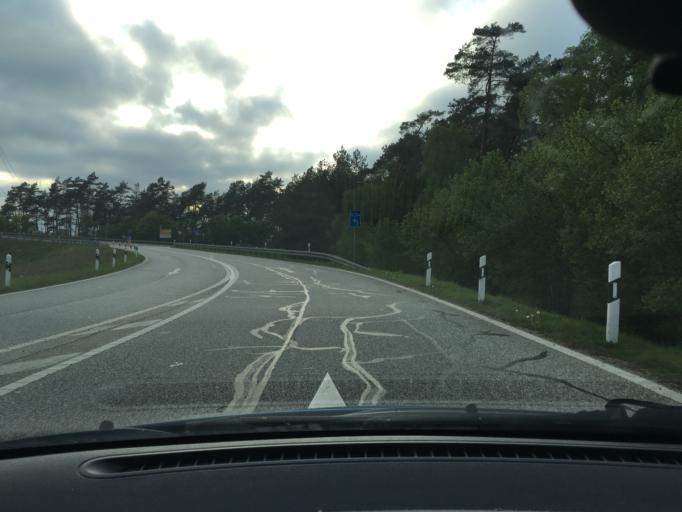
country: DE
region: Mecklenburg-Vorpommern
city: Zarrentin
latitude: 53.5124
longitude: 10.8968
